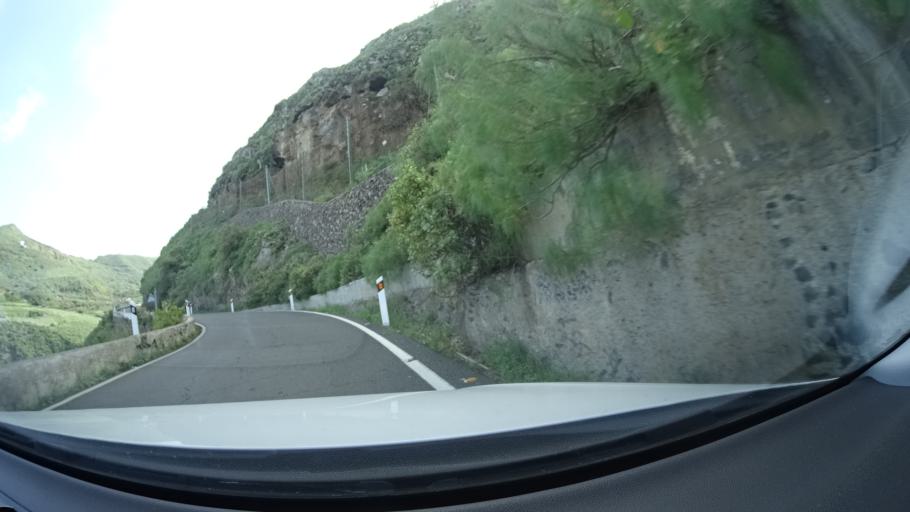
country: ES
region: Canary Islands
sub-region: Provincia de Las Palmas
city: Guia
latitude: 28.1130
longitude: -15.6414
